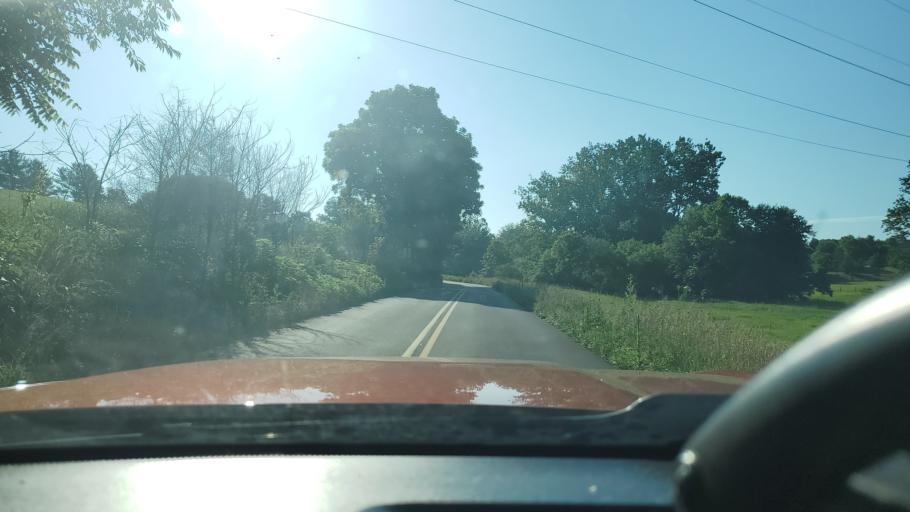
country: US
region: Pennsylvania
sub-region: Montgomery County
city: Harleysville
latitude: 40.2988
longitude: -75.3973
